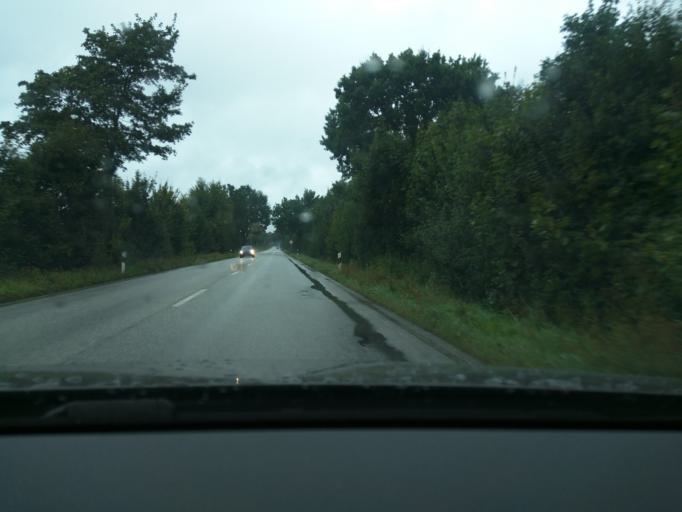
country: DE
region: Schleswig-Holstein
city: Kruzen
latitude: 53.4073
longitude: 10.5380
